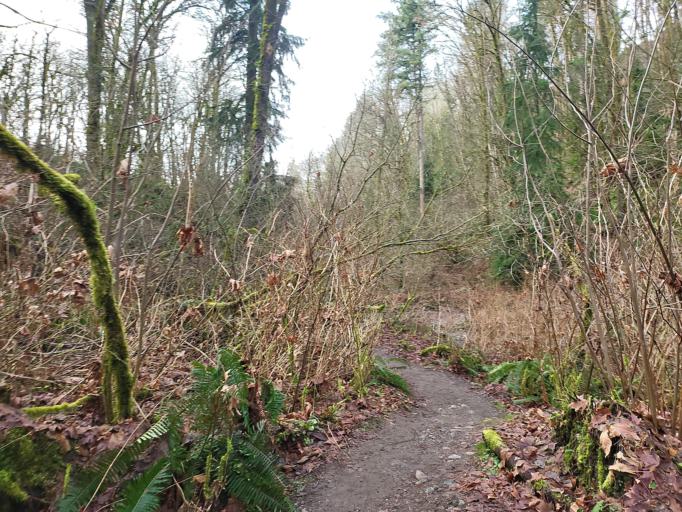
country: US
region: Washington
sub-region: King County
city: Newcastle
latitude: 47.5443
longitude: -122.1558
